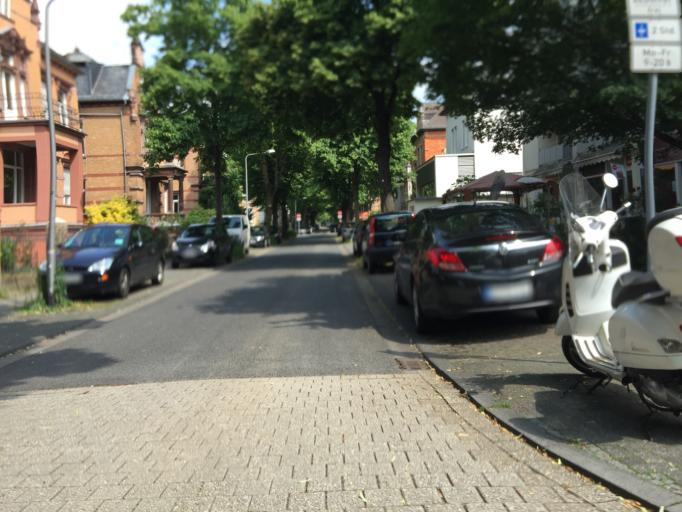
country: DE
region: Hesse
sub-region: Regierungsbezirk Darmstadt
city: Wiesbaden
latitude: 50.0727
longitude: 8.2502
